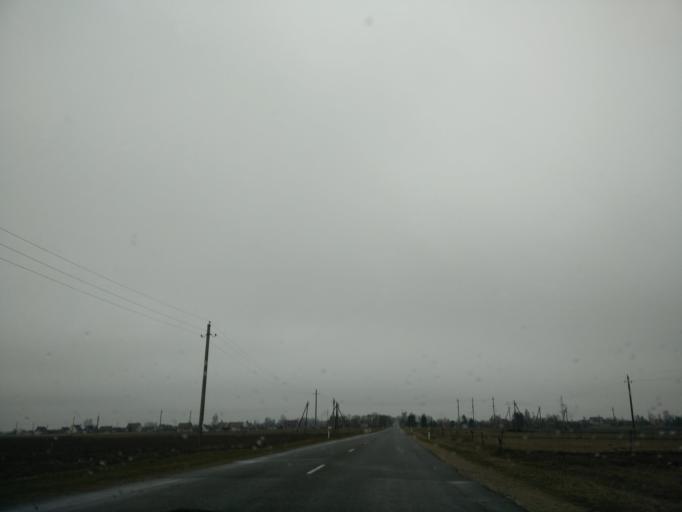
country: LT
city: Ariogala
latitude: 55.3543
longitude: 23.3786
